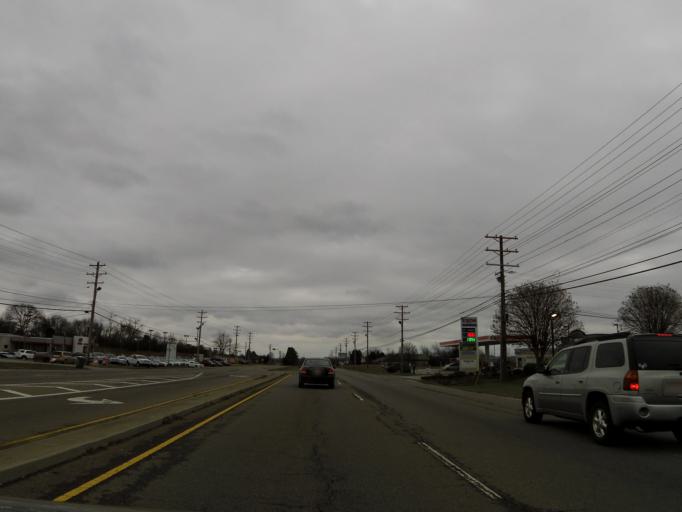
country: US
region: Tennessee
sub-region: Hamblen County
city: Morristown
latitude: 36.1788
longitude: -83.3918
